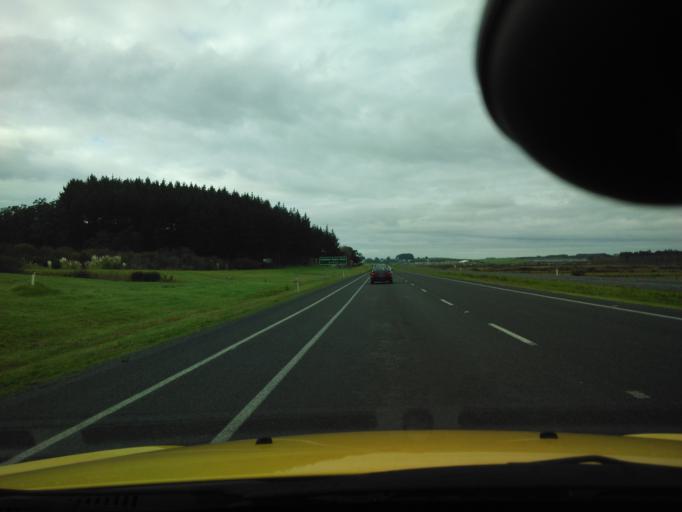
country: NZ
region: Waikato
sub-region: Waikato District
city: Te Kauwhata
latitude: -37.3406
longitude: 175.0647
